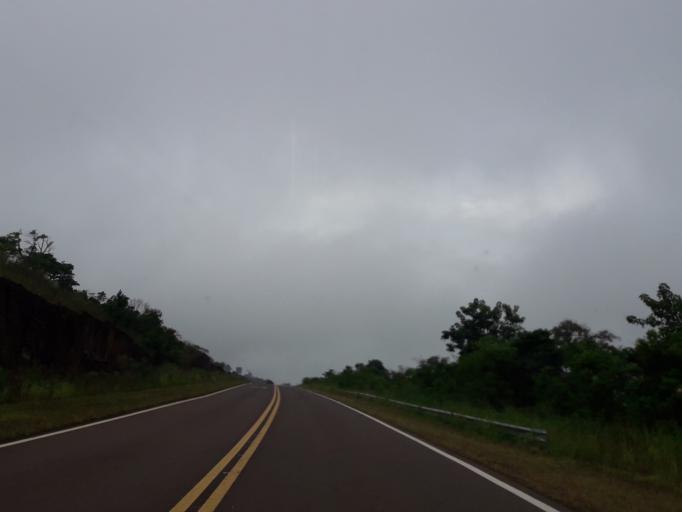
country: AR
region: Misiones
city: Bernardo de Irigoyen
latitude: -26.4100
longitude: -53.8235
